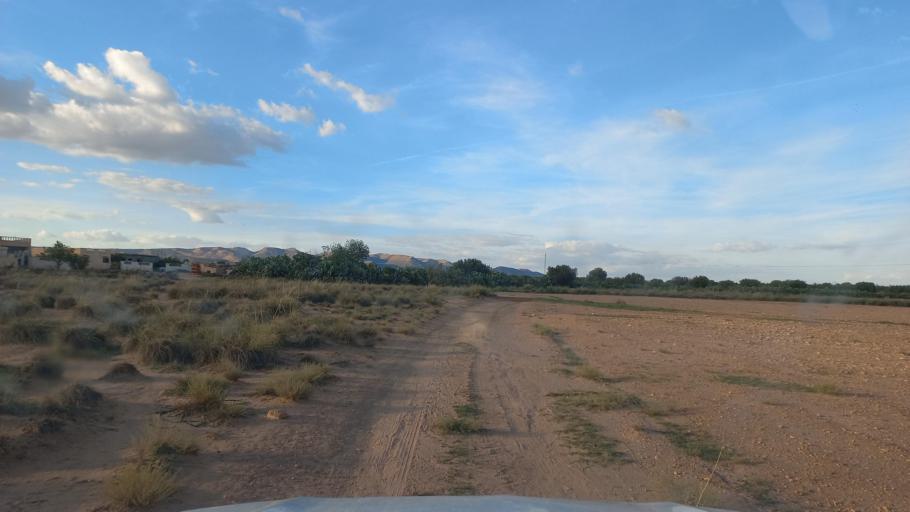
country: TN
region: Al Qasrayn
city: Sbiba
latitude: 35.3529
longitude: 9.0370
